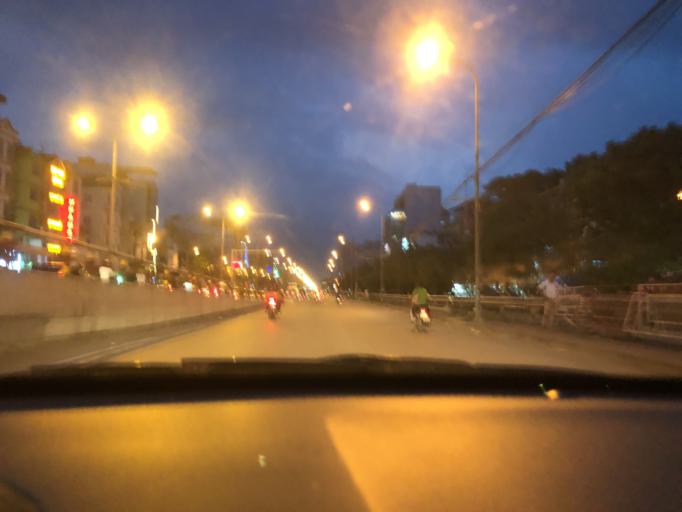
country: VN
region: Ha Noi
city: Hai BaTrung
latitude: 20.9961
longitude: 105.8411
